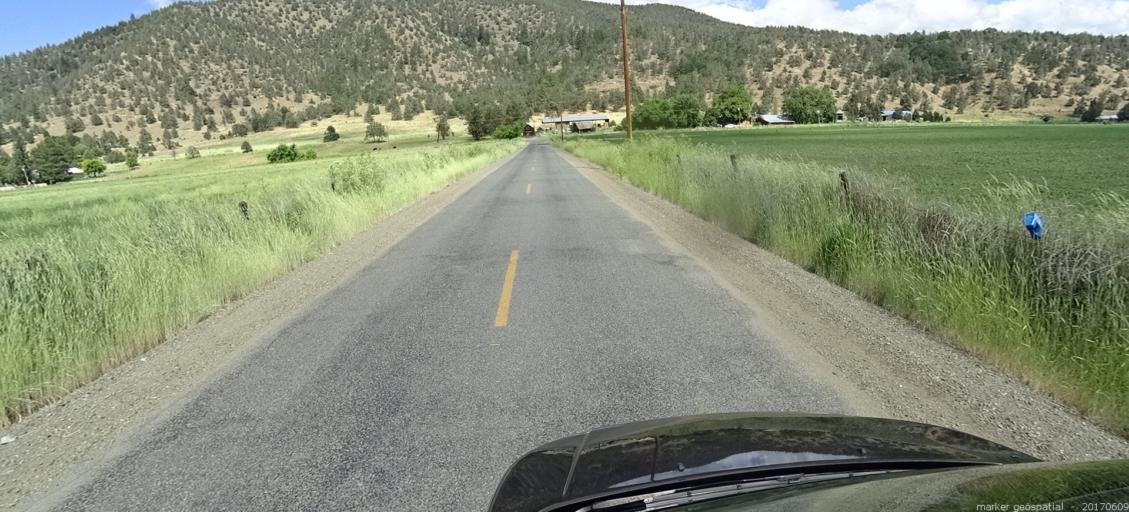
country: US
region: California
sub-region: Siskiyou County
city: Yreka
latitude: 41.5195
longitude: -122.8441
